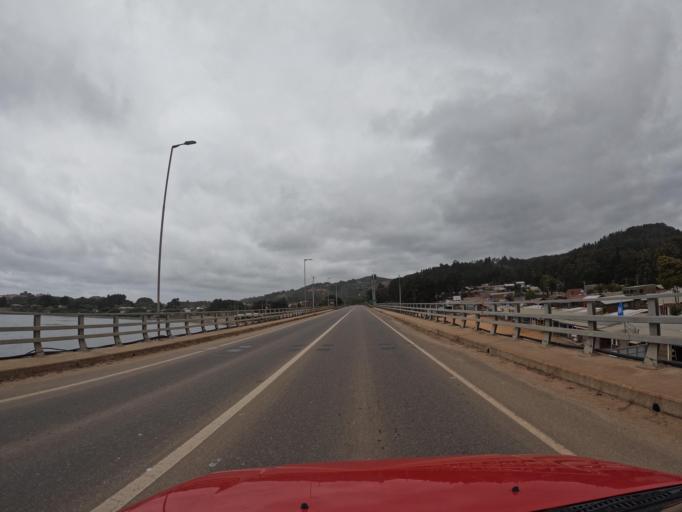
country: CL
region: O'Higgins
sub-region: Provincia de Colchagua
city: Santa Cruz
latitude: -34.4797
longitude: -72.0179
